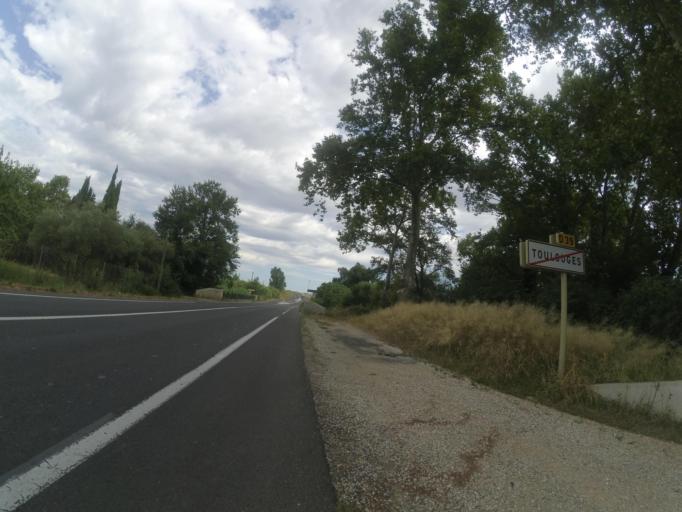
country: FR
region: Languedoc-Roussillon
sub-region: Departement des Pyrenees-Orientales
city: Toulouges
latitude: 42.6764
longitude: 2.8243
